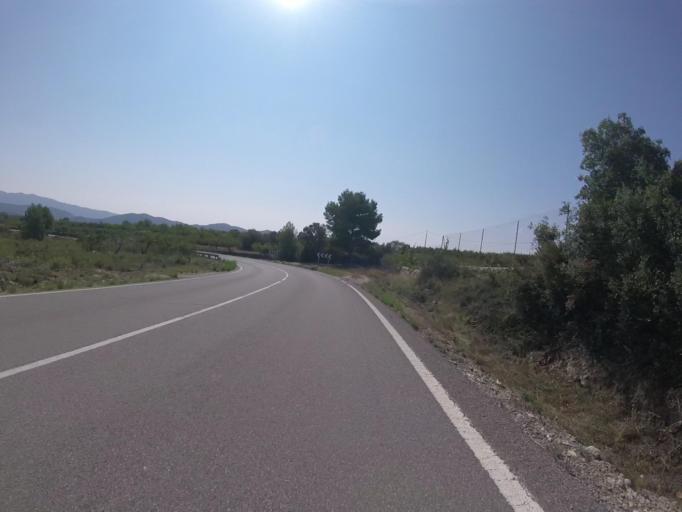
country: ES
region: Valencia
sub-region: Provincia de Castello
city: Adzaneta
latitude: 40.2369
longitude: -0.1887
